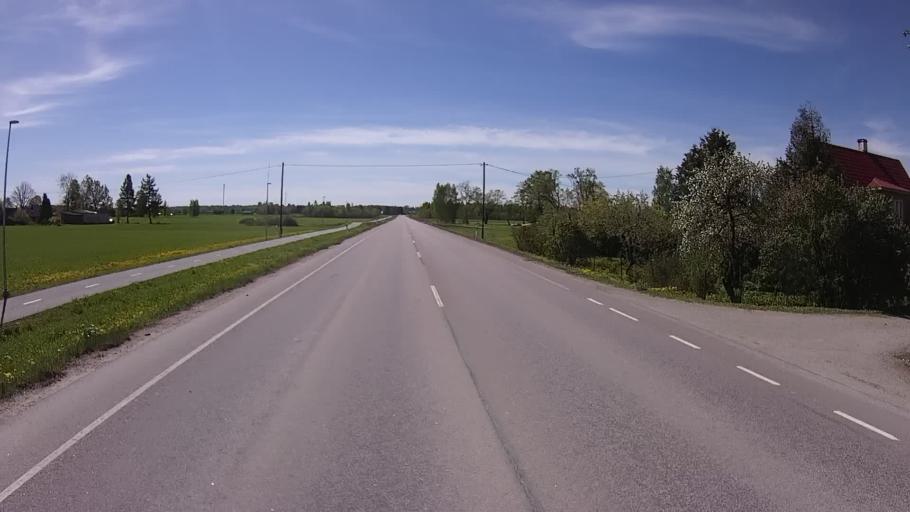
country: EE
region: Polvamaa
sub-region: Polva linn
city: Polva
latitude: 58.0814
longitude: 27.0900
